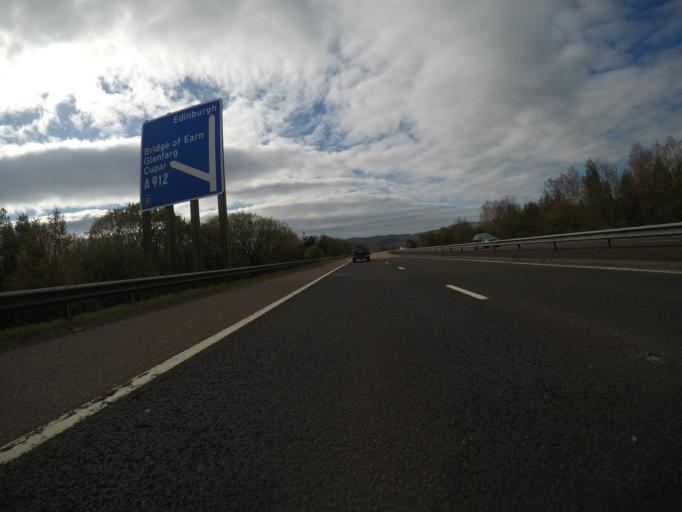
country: GB
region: Scotland
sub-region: Perth and Kinross
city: Bridge of Earn
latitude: 56.3480
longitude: -3.3967
